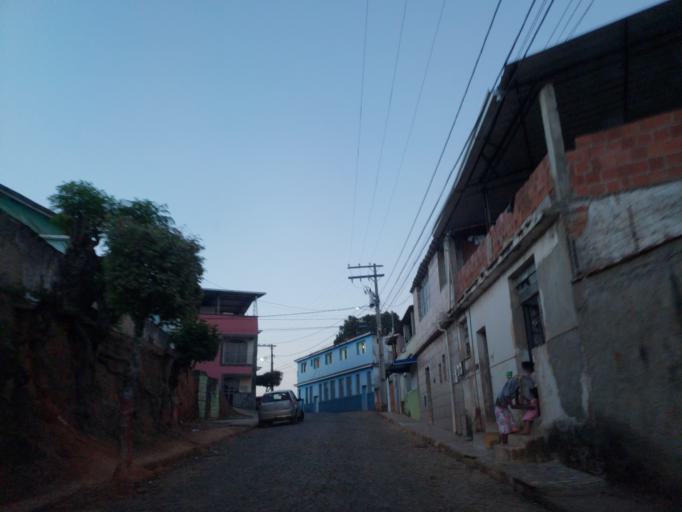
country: BR
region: Minas Gerais
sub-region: Sao Joao Nepomuceno
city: Sao Joao Nepomuceno
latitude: -21.5195
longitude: -43.0142
